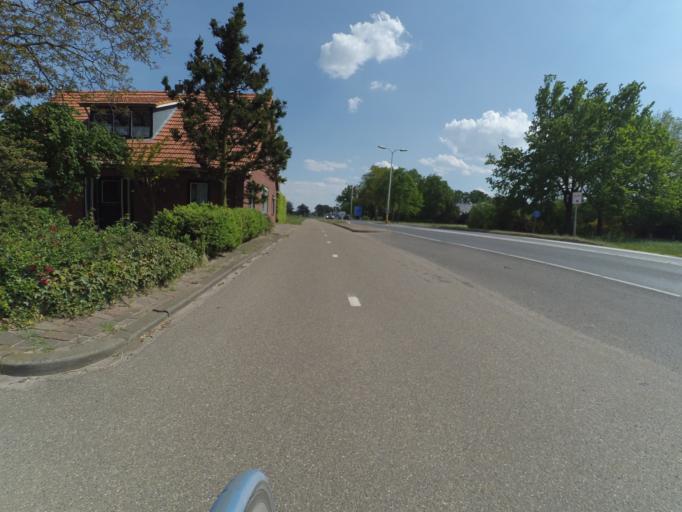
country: NL
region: Overijssel
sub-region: Gemeente Oldenzaal
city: Oldenzaal
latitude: 52.3456
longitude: 6.8601
